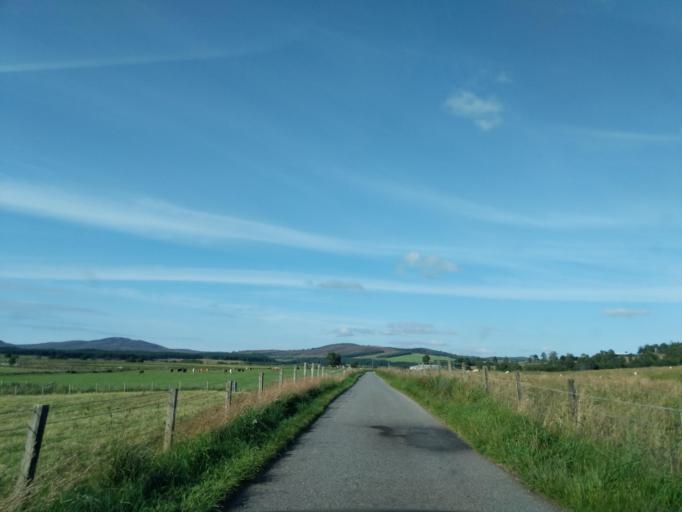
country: GB
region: Scotland
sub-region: Highland
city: Grantown on Spey
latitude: 57.2887
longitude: -3.7248
